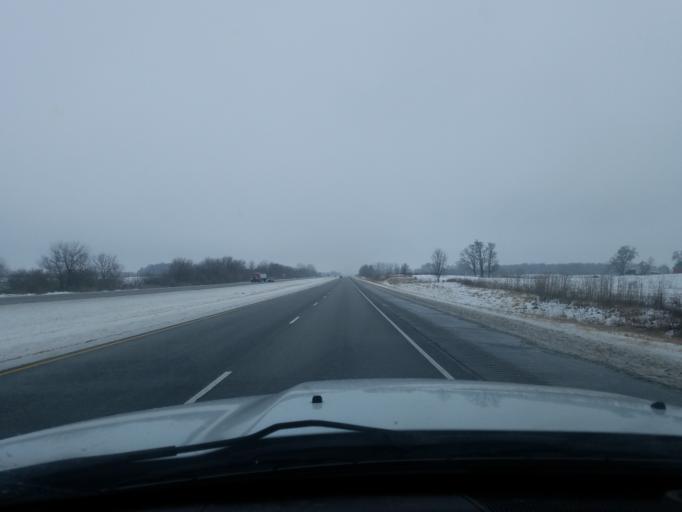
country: US
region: Indiana
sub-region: Fulton County
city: Rochester
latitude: 40.9471
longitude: -86.1683
